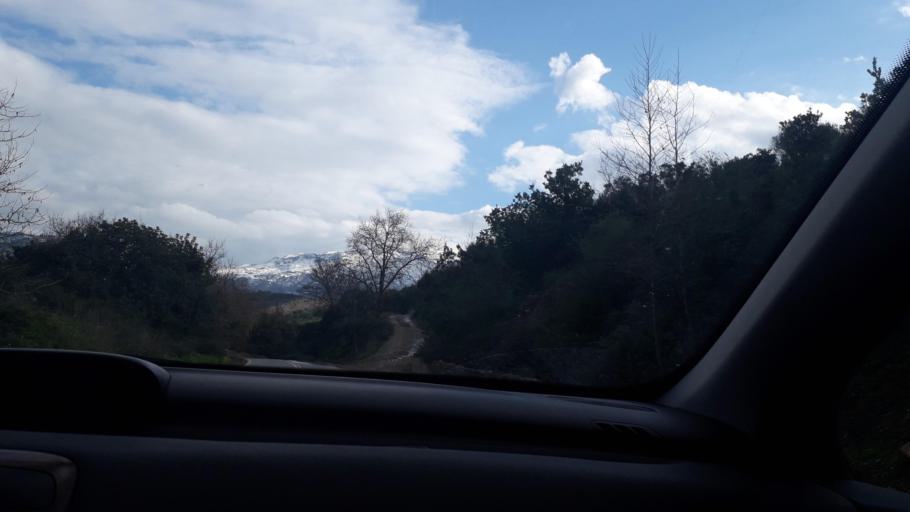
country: GR
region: Crete
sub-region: Nomos Rethymnis
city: Agia Foteini
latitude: 35.2952
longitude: 24.5538
